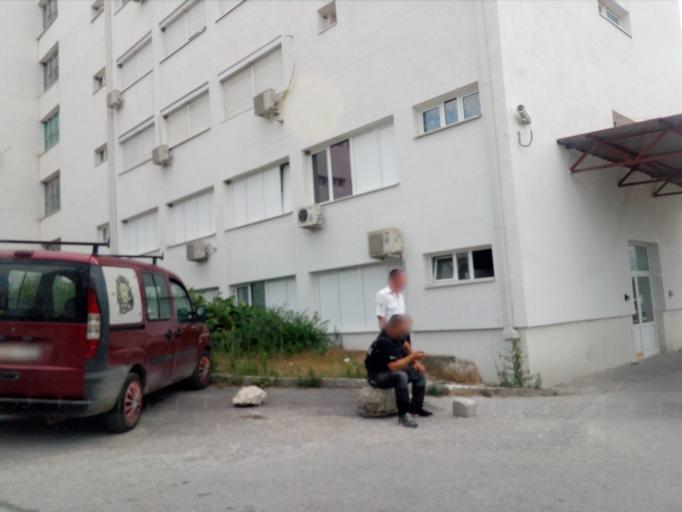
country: MK
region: Veles
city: Veles
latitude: 41.7155
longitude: 21.7761
